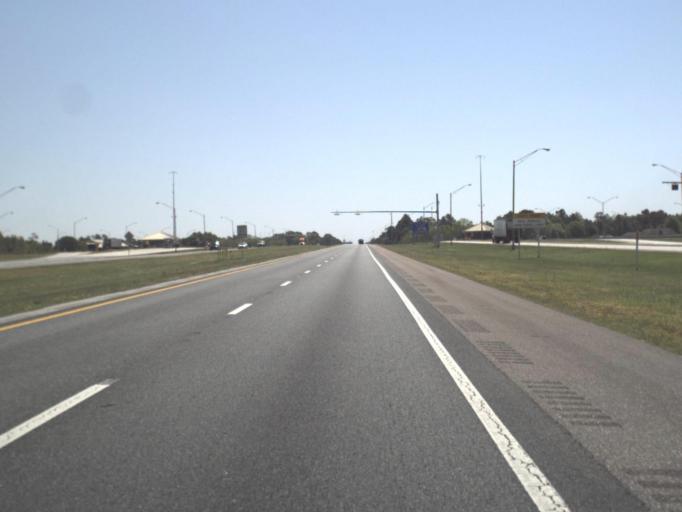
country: US
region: Florida
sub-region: Escambia County
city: Cantonment
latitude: 30.5555
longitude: -87.3656
